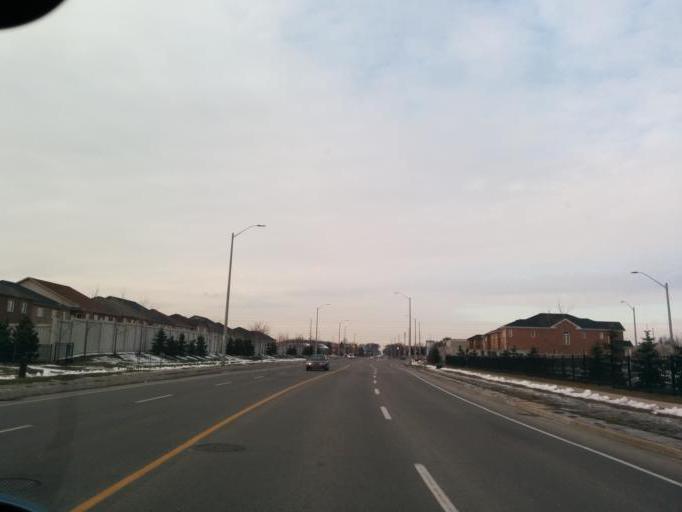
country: CA
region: Ontario
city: Mississauga
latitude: 43.5953
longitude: -79.6610
